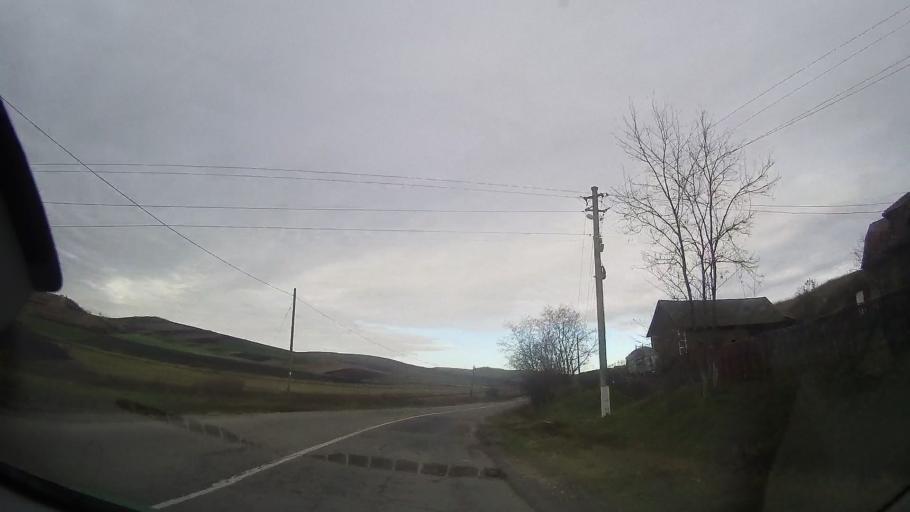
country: RO
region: Cluj
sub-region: Comuna Camarasu
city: Camarasu
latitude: 46.8039
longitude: 24.1473
